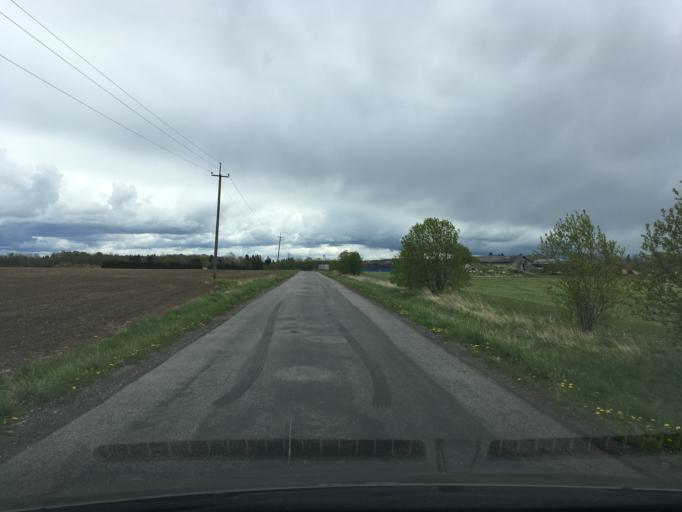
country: EE
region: Harju
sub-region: Rae vald
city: Jueri
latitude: 59.3677
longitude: 24.9621
